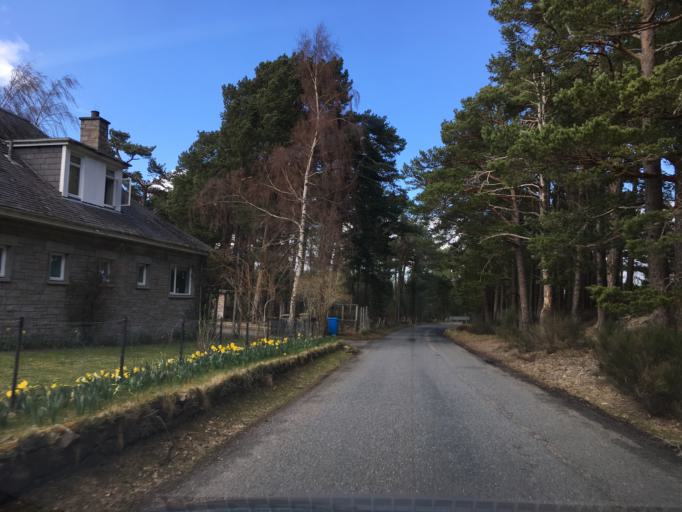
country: GB
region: Scotland
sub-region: Highland
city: Aviemore
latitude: 57.1776
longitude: -3.7973
